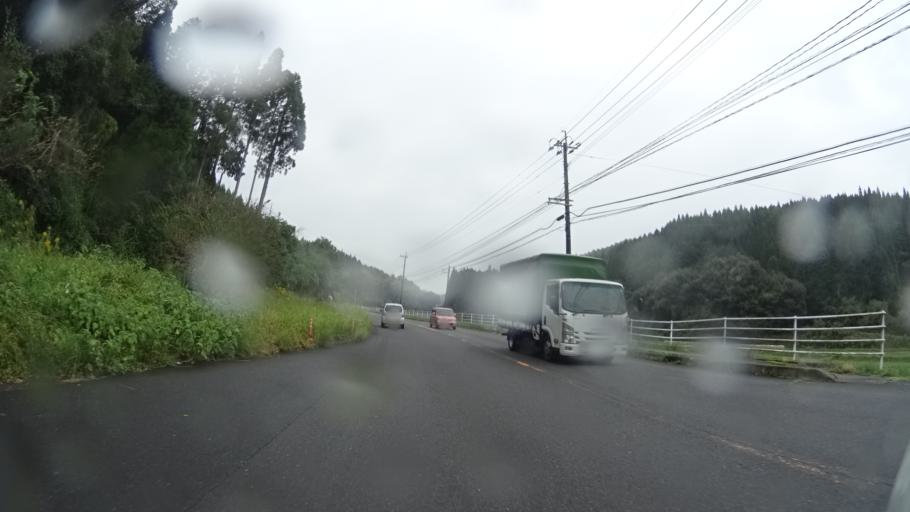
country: JP
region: Kagoshima
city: Kajiki
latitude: 31.8198
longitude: 130.6772
